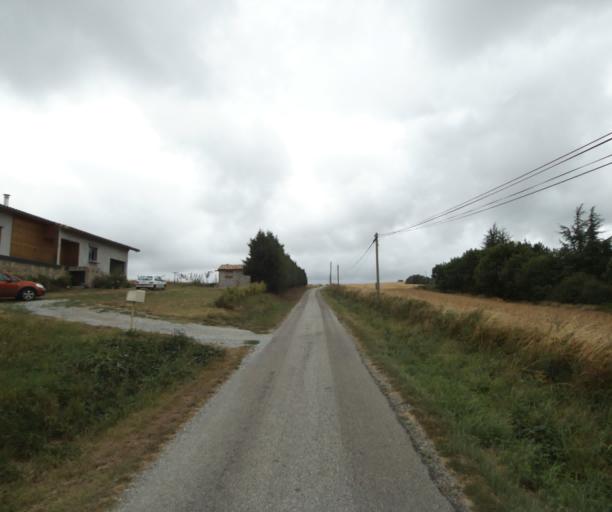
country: FR
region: Midi-Pyrenees
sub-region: Departement du Tarn
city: Soreze
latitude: 43.3906
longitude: 2.0448
